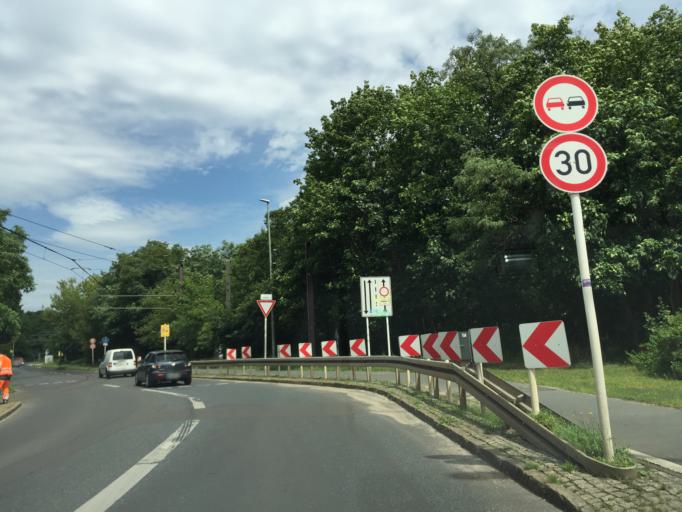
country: DE
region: Berlin
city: Mahlsdorf
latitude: 52.4986
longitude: 13.6133
